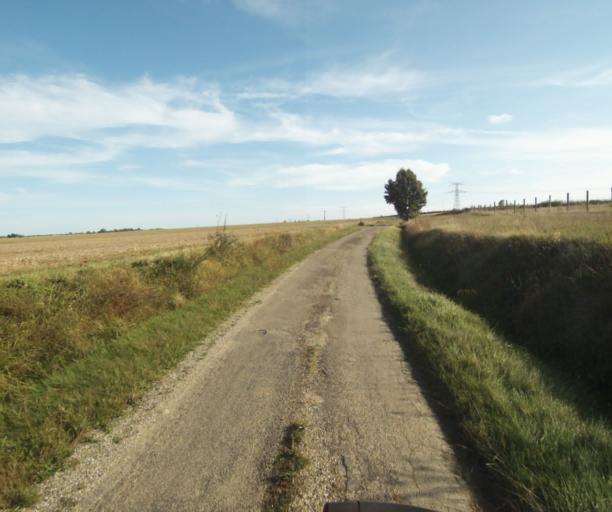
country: FR
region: Midi-Pyrenees
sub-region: Departement du Tarn-et-Garonne
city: Finhan
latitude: 43.9094
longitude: 1.1110
